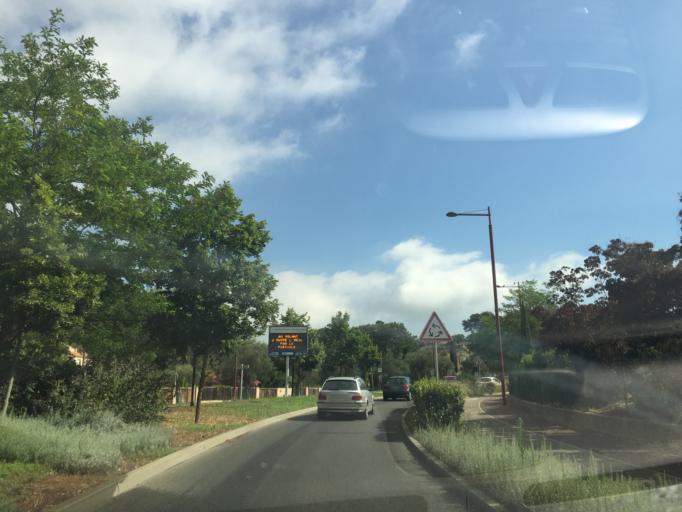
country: FR
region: Provence-Alpes-Cote d'Azur
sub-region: Departement des Alpes-Maritimes
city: Vallauris
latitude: 43.5851
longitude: 7.0900
